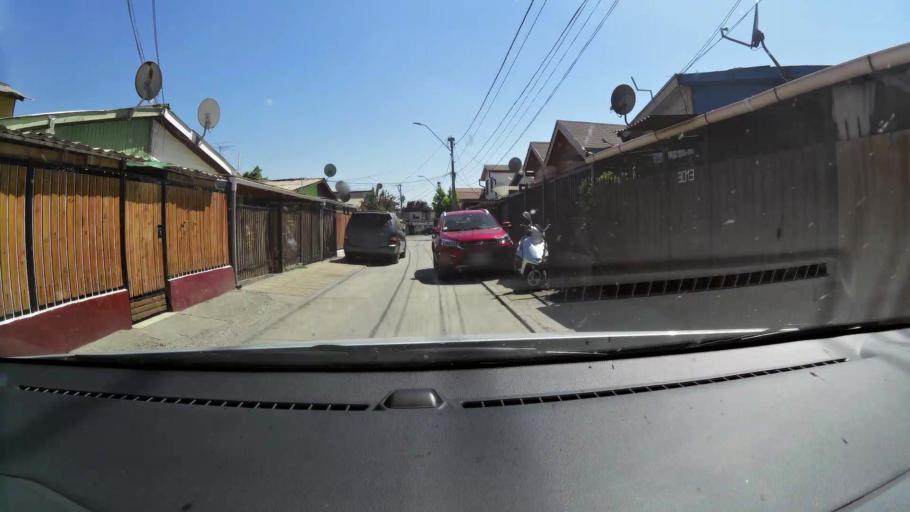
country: CL
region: Santiago Metropolitan
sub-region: Provincia de Maipo
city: San Bernardo
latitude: -33.6272
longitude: -70.6983
